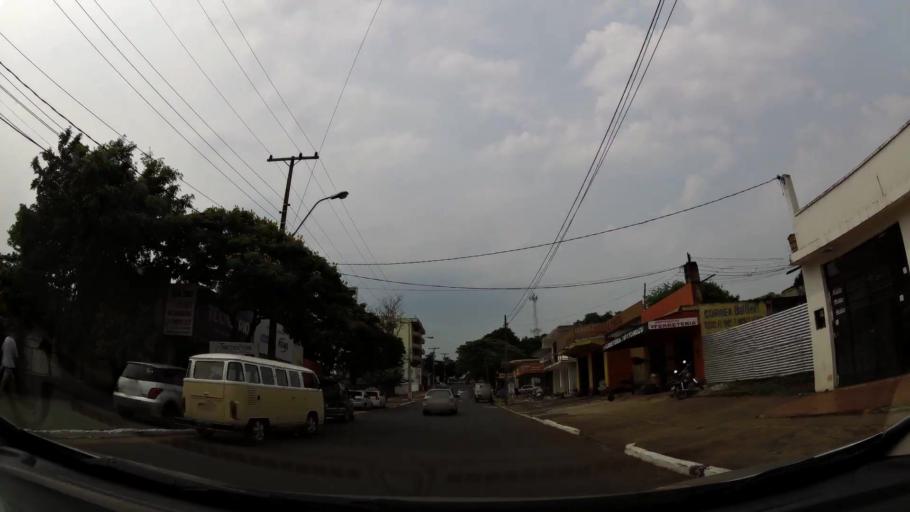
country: BR
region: Parana
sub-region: Foz Do Iguacu
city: Foz do Iguacu
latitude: -25.5525
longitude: -54.6076
